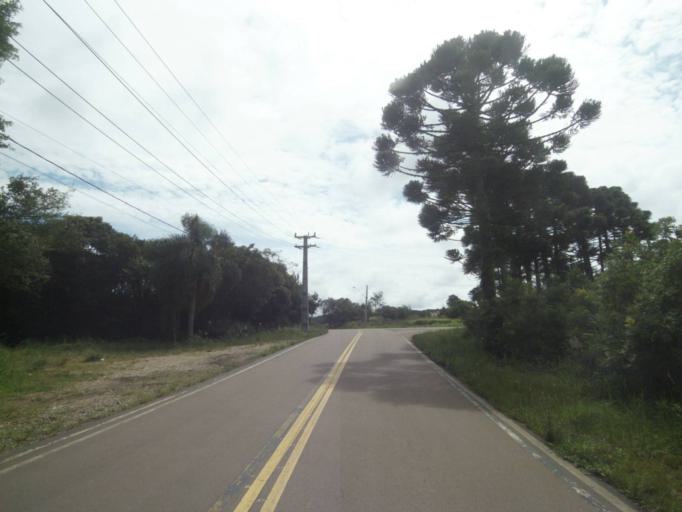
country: BR
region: Parana
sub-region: Campina Grande Do Sul
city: Campina Grande do Sul
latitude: -25.3146
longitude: -49.0209
